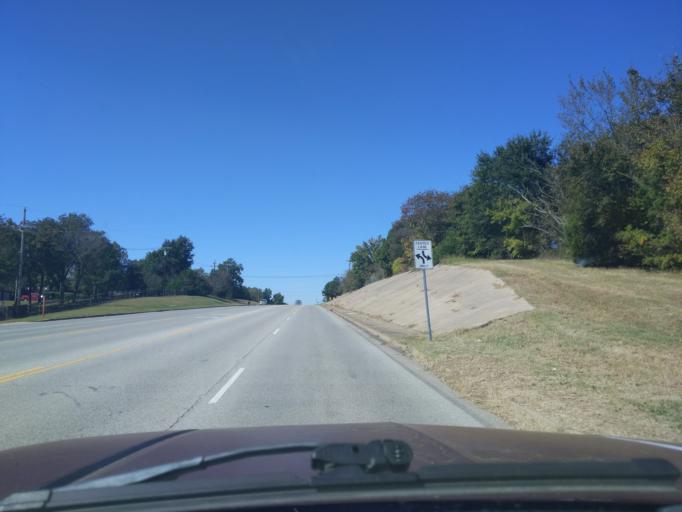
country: US
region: Oklahoma
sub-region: Creek County
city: Kiefer
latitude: 35.9885
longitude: -96.0662
